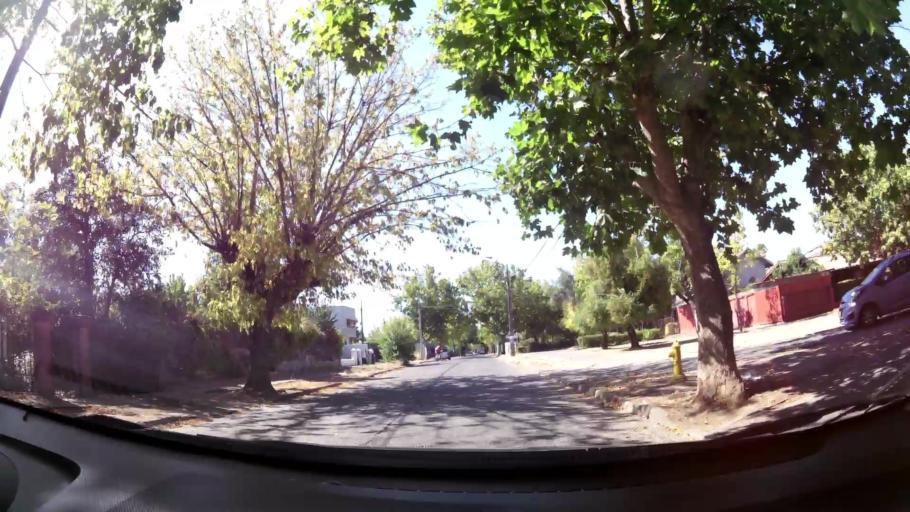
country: CL
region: Maule
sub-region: Provincia de Talca
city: Talca
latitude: -35.4341
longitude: -71.6620
